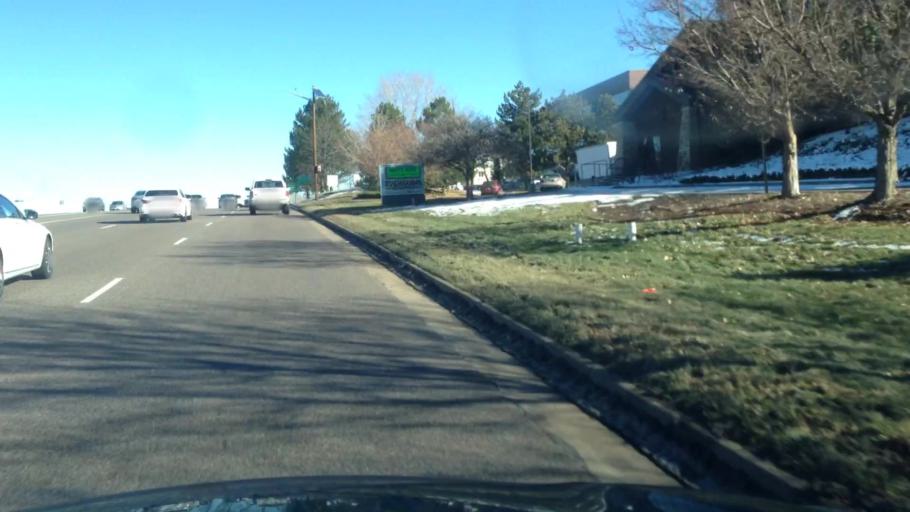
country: US
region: Colorado
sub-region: Arapahoe County
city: Dove Valley
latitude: 39.5949
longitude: -104.8369
